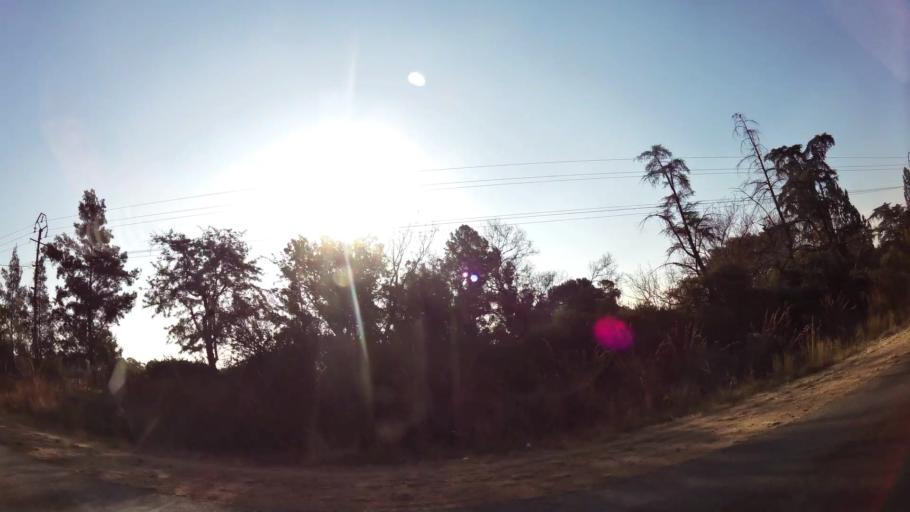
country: ZA
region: Gauteng
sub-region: West Rand District Municipality
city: Muldersdriseloop
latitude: -26.0173
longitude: 27.8842
